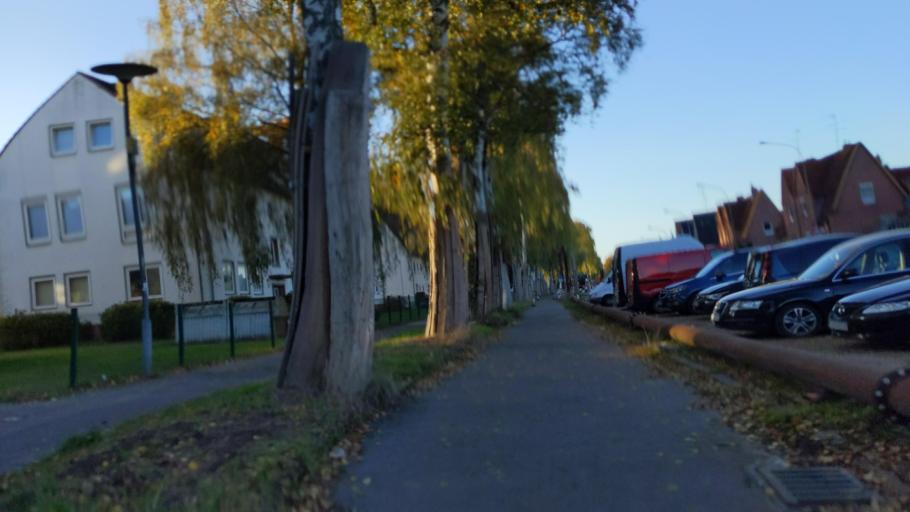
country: DE
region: Schleswig-Holstein
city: Luebeck
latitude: 53.8594
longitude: 10.7305
